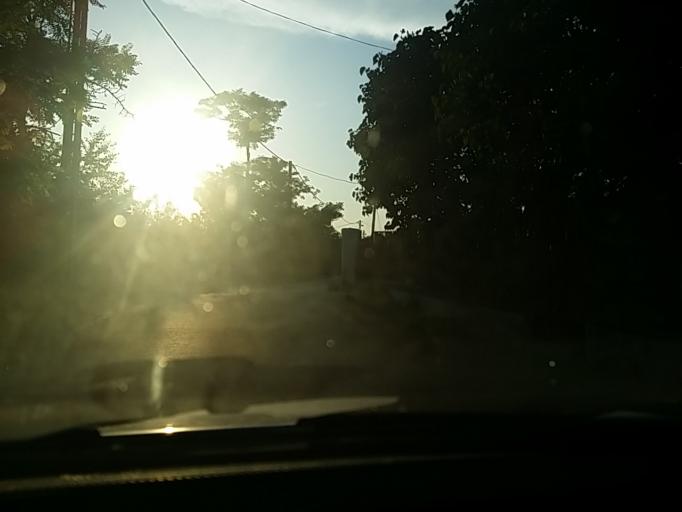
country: HU
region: Pest
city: Urom
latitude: 47.5775
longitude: 19.0225
